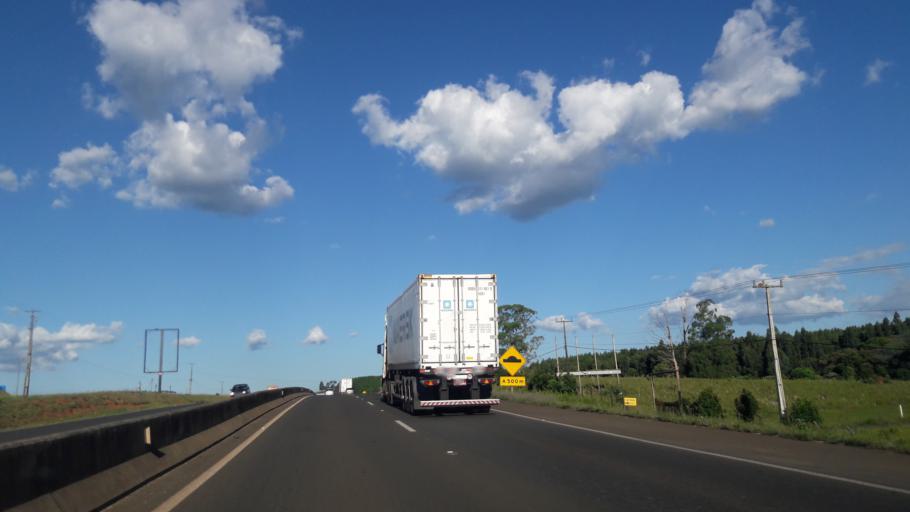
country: BR
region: Parana
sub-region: Guarapuava
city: Guarapuava
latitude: -25.3465
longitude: -51.4479
